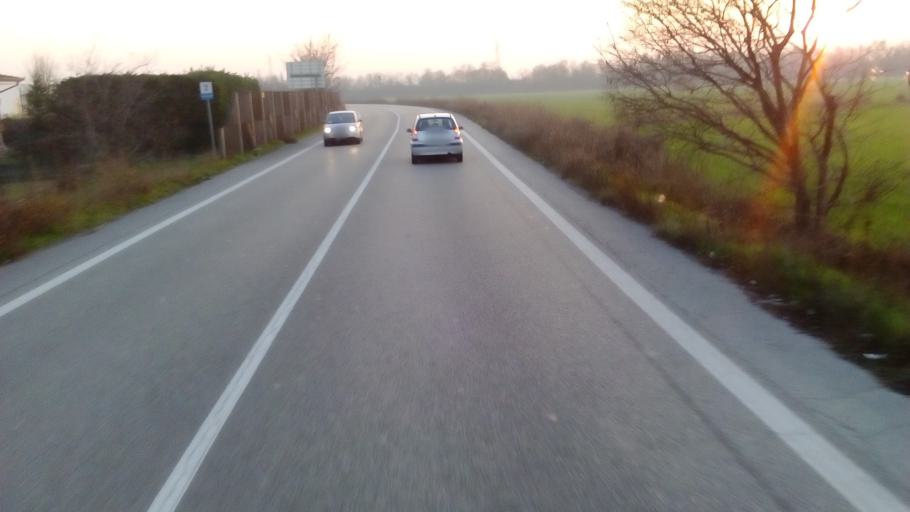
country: IT
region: Lombardy
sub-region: Provincia di Brescia
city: Novagli
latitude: 45.3974
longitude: 10.4606
